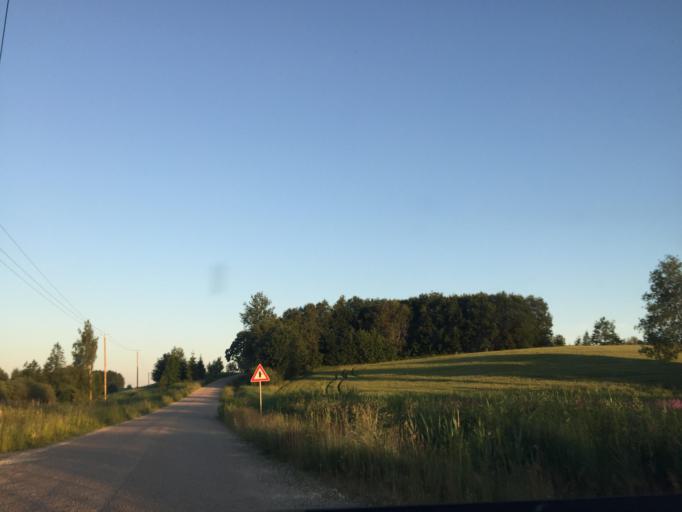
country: LV
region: Rezekne
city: Rezekne
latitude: 56.3660
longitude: 27.4105
